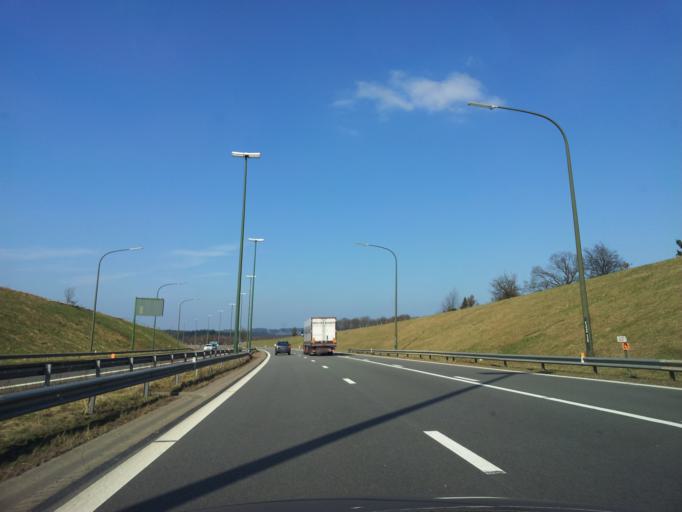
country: BE
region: Wallonia
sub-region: Province de Liege
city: Jalhay
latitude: 50.5170
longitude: 5.9454
